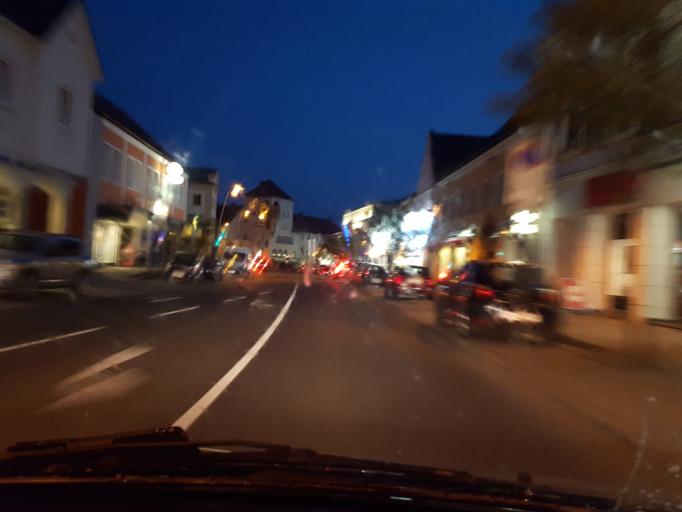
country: AT
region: Lower Austria
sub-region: Politischer Bezirk Scheibbs
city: Wieselburg
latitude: 48.1318
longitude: 15.1393
